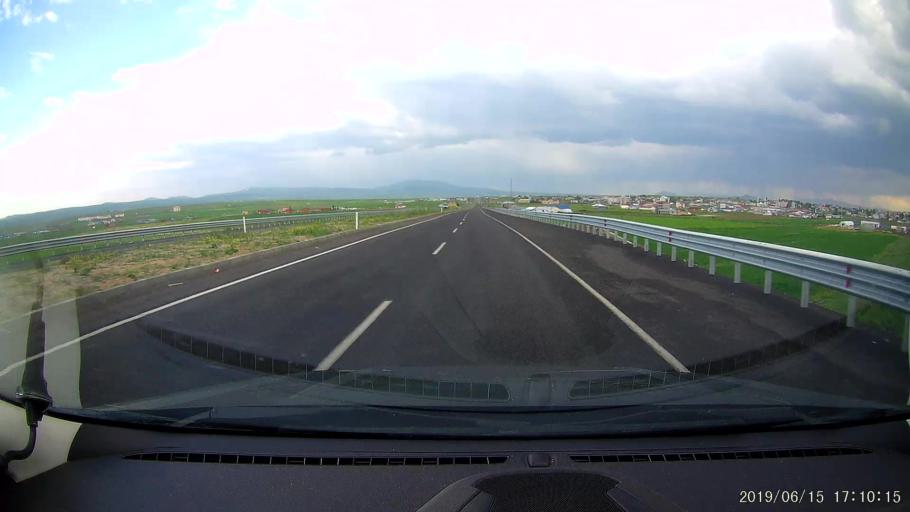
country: TR
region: Kars
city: Kars
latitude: 40.6243
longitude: 43.1338
